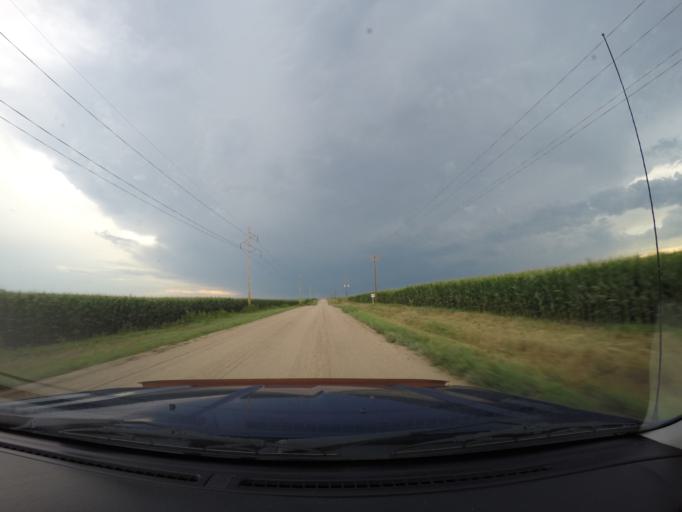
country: US
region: Nebraska
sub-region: Buffalo County
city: Kearney
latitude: 40.8441
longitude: -99.1258
